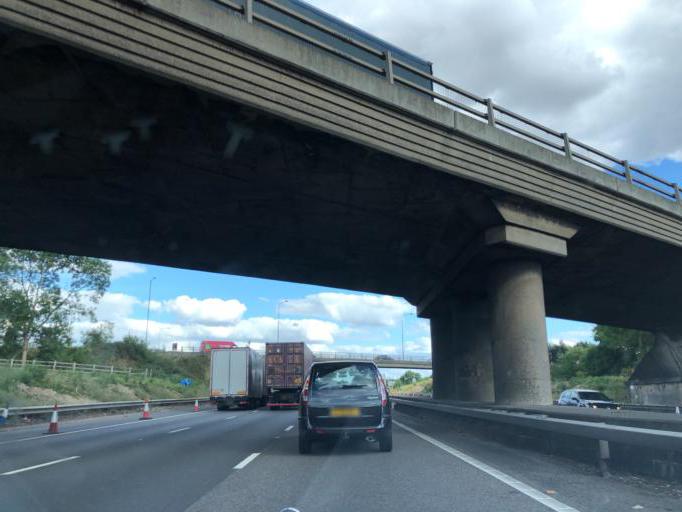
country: GB
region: England
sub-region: Milton Keynes
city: Broughton
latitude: 52.0594
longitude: -0.7014
